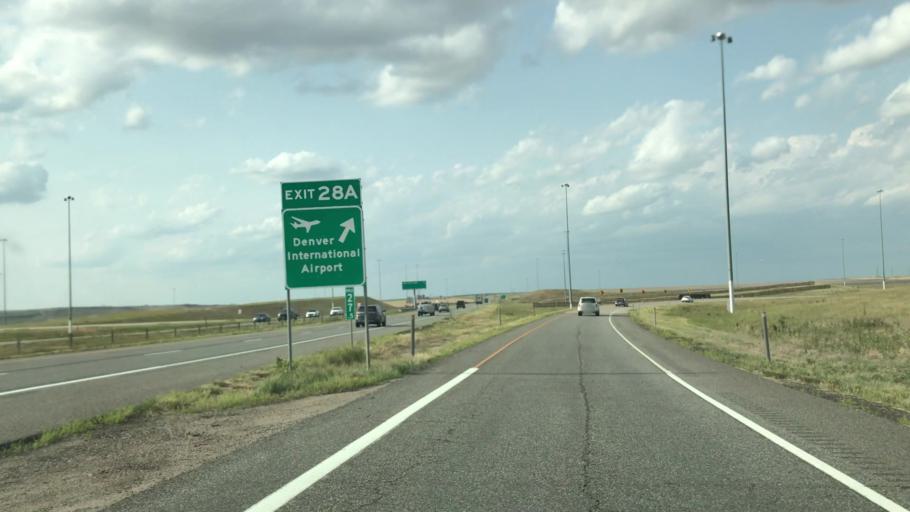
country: US
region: Colorado
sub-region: Adams County
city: Aurora
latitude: 39.8283
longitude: -104.7468
